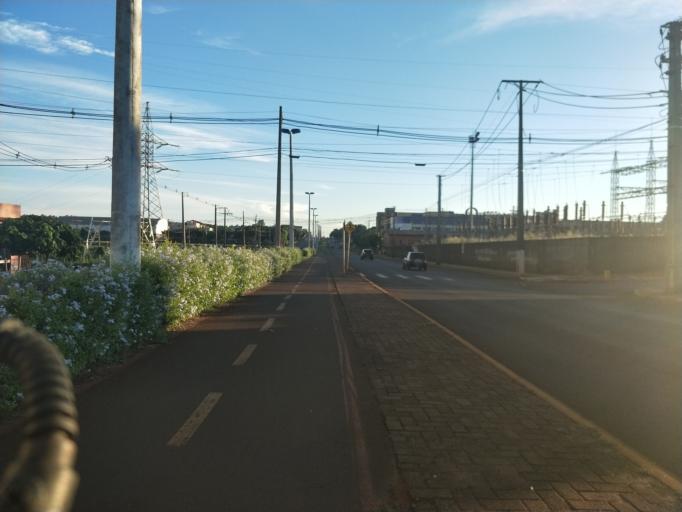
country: BR
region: Parana
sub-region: Marechal Candido Rondon
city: Marechal Candido Rondon
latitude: -24.5548
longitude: -54.0472
